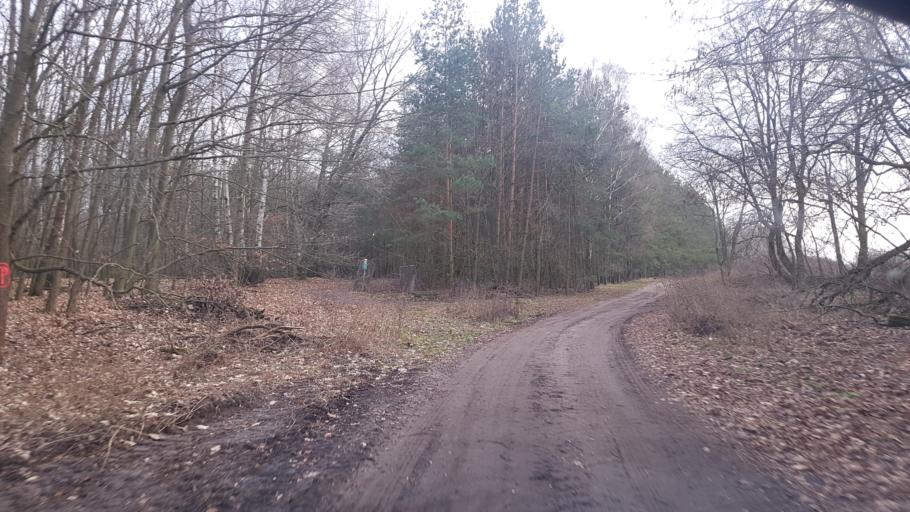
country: DE
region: Brandenburg
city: Ludwigsfelde
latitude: 52.3358
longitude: 13.2221
